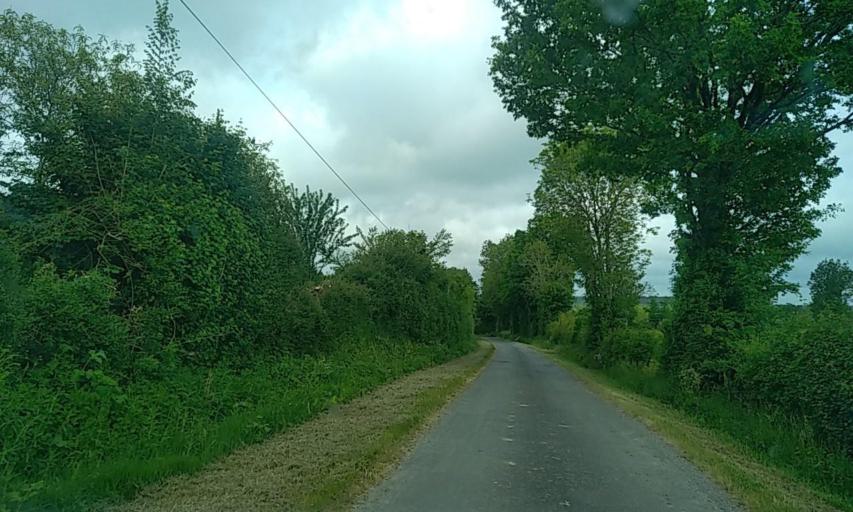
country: FR
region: Poitou-Charentes
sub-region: Departement des Deux-Sevres
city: Boisme
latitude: 46.7654
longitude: -0.4203
